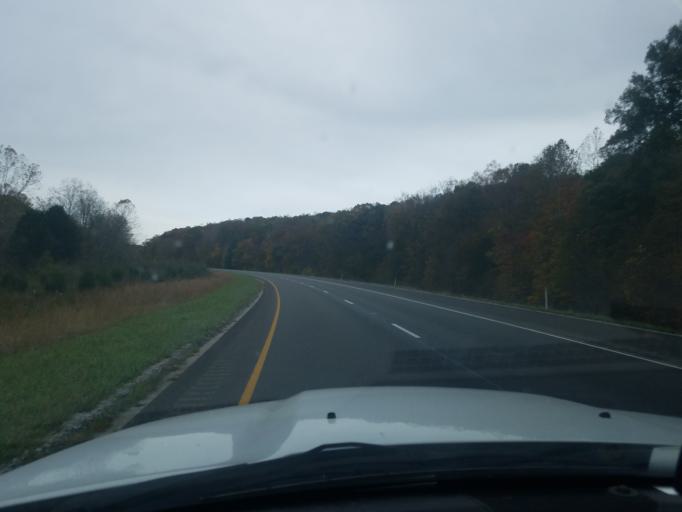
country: US
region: Indiana
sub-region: Crawford County
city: English
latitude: 38.2379
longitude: -86.4039
